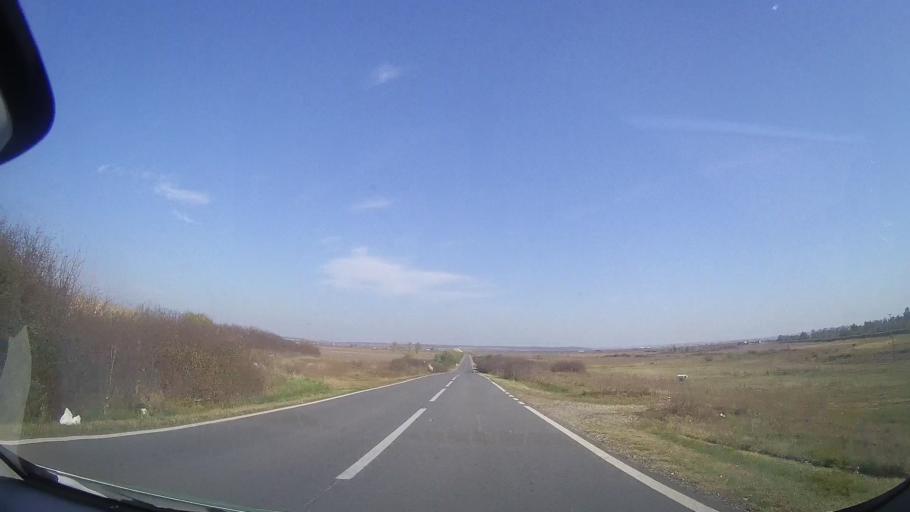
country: RO
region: Timis
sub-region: Comuna Belint
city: Belint
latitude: 45.7677
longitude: 21.7287
